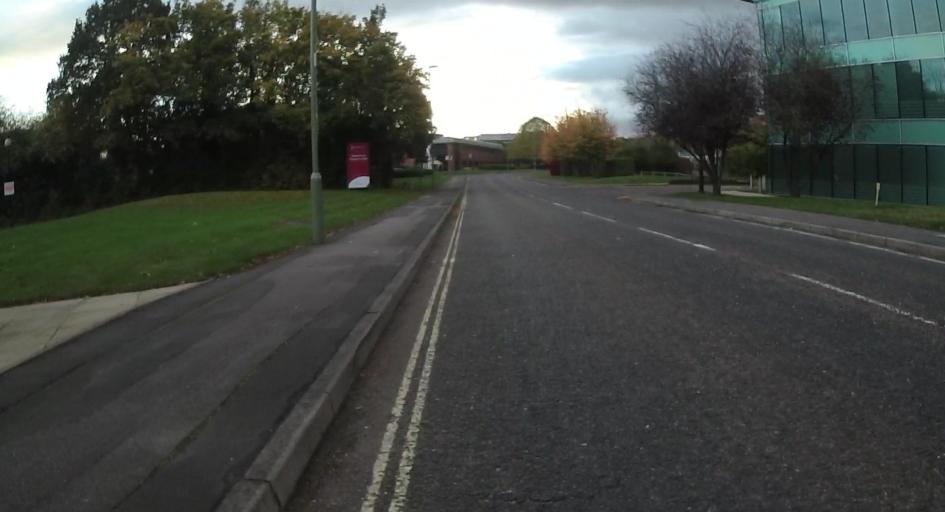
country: GB
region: England
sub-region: Hampshire
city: Basingstoke
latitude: 51.2947
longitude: -1.0656
